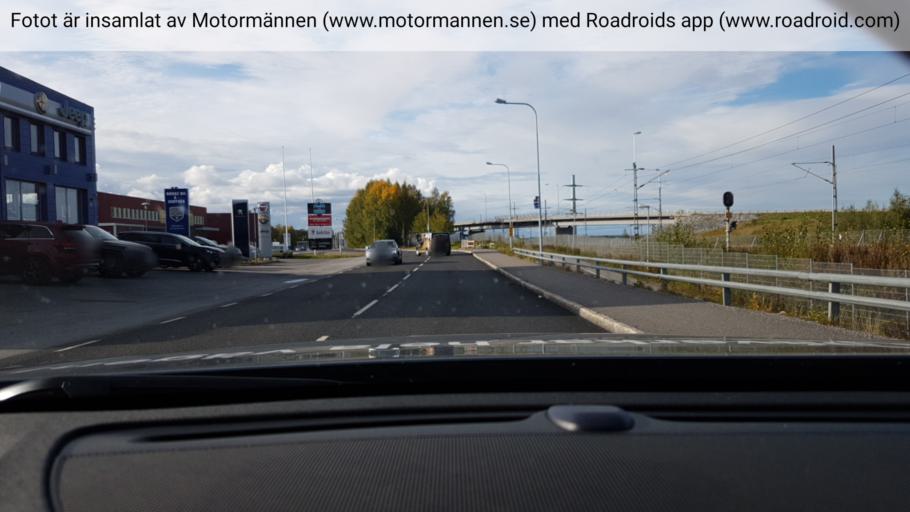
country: SE
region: Norrbotten
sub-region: Lulea Kommun
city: Bergnaset
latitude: 65.6118
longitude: 22.1144
